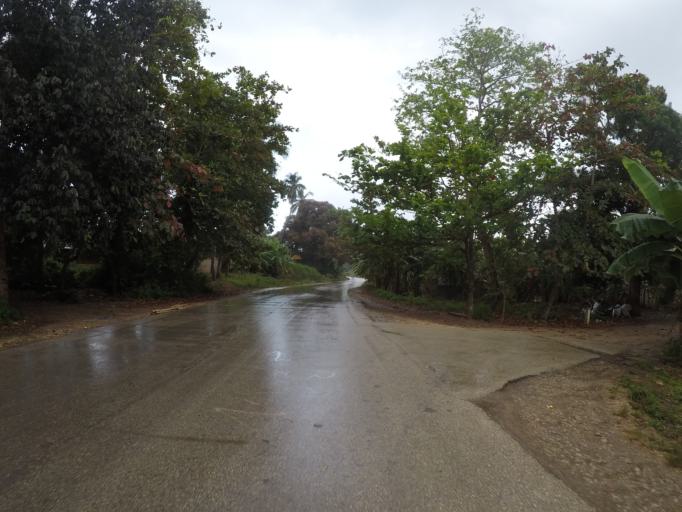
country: TZ
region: Zanzibar North
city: Mkokotoni
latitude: -5.9594
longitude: 39.1951
